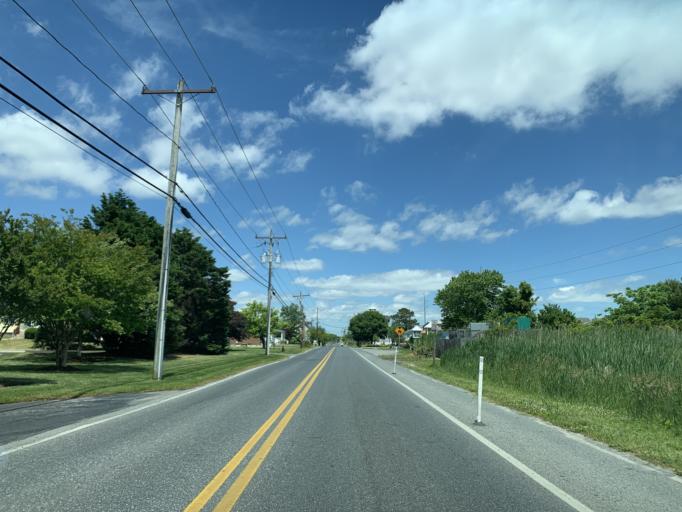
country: US
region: Maryland
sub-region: Worcester County
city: West Ocean City
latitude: 38.3293
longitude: -75.1072
